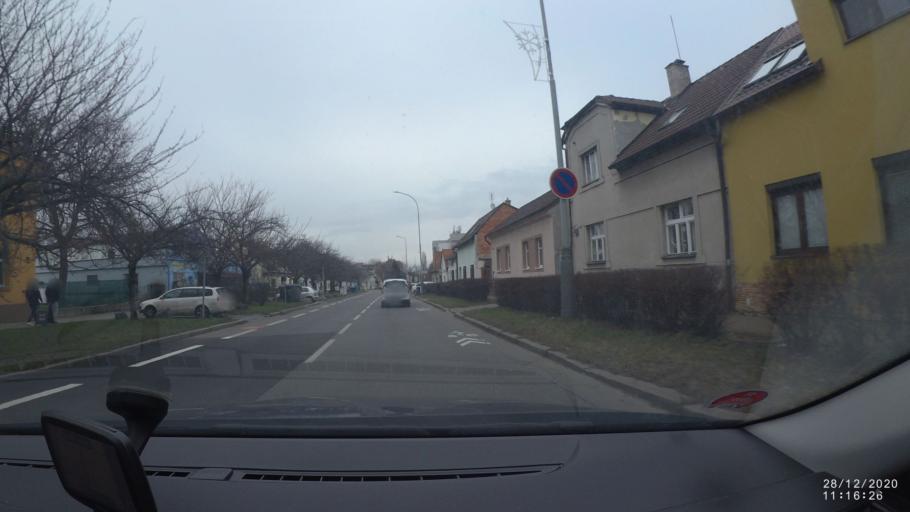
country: CZ
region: Praha
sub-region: Praha 18
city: Letnany
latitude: 50.1359
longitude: 14.5142
